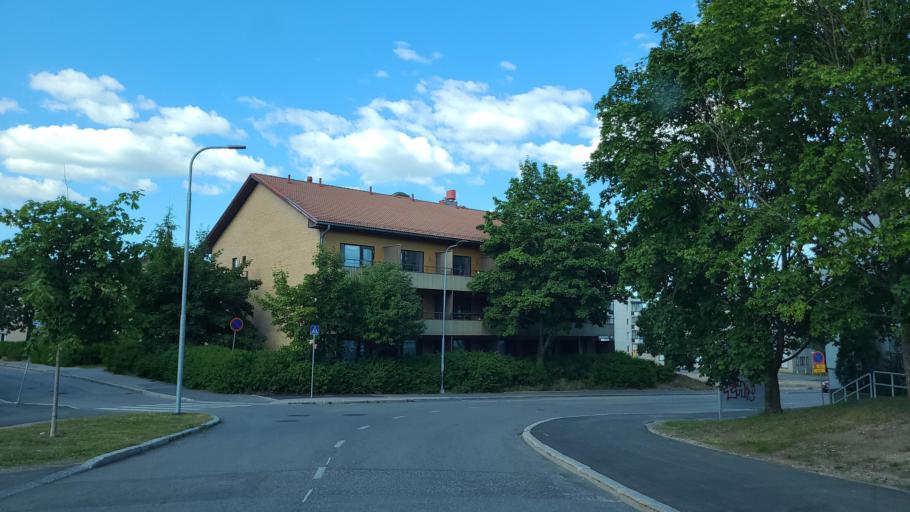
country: FI
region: Central Finland
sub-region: Jyvaeskylae
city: Jyvaeskylae
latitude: 62.2477
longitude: 25.7415
